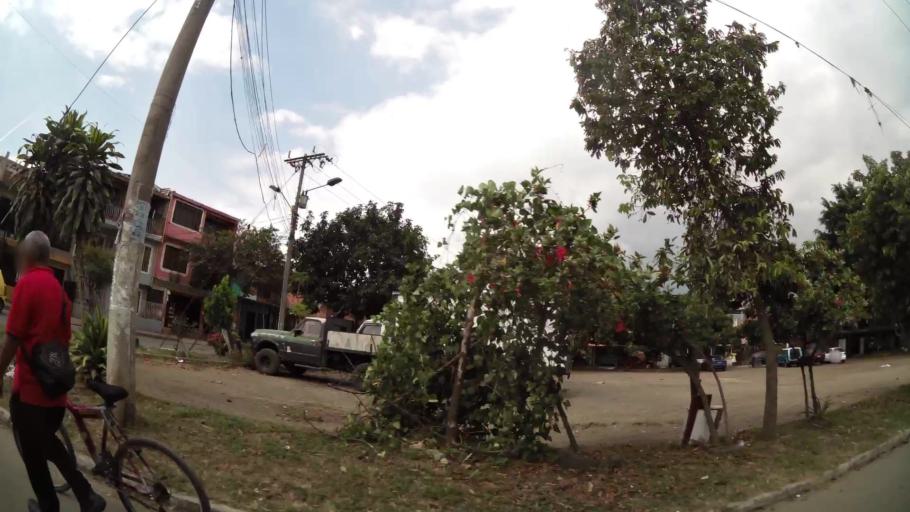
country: CO
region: Valle del Cauca
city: Cali
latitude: 3.4944
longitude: -76.4852
